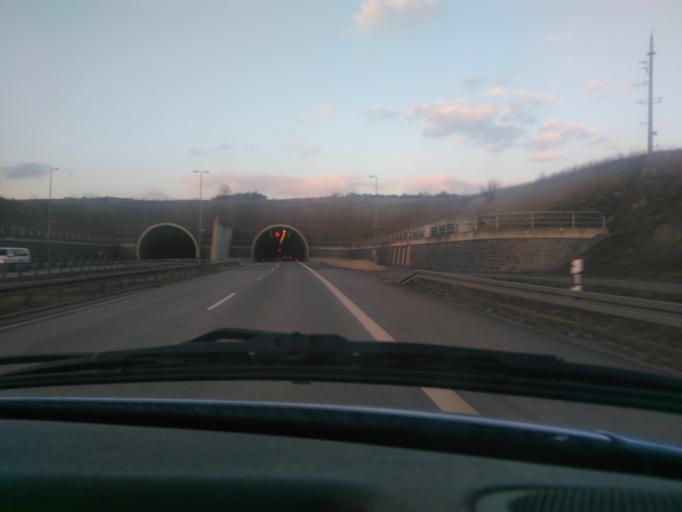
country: DE
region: Thuringia
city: Hemleben
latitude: 51.2699
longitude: 11.2134
